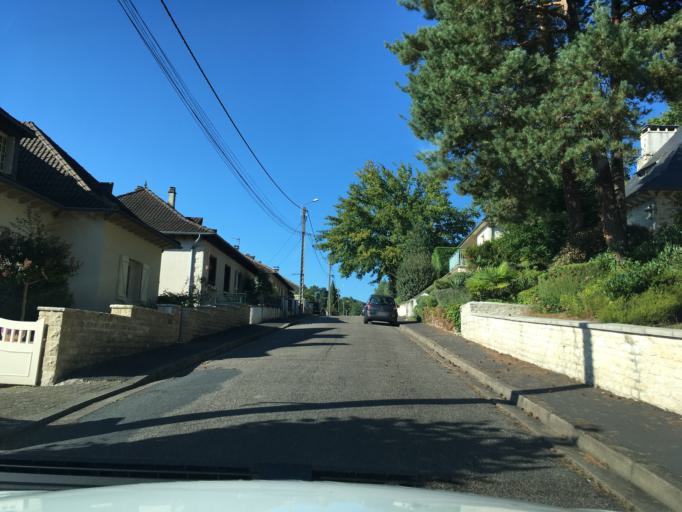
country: FR
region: Limousin
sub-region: Departement de la Correze
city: Malemort-sur-Correze
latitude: 45.1742
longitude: 1.5471
